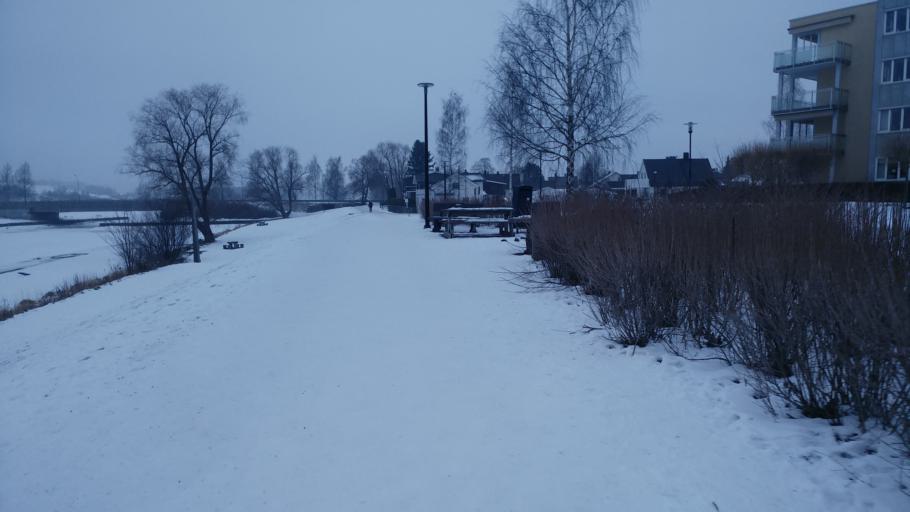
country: NO
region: Akershus
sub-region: Skedsmo
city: Lillestrom
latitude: 59.9557
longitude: 11.0318
